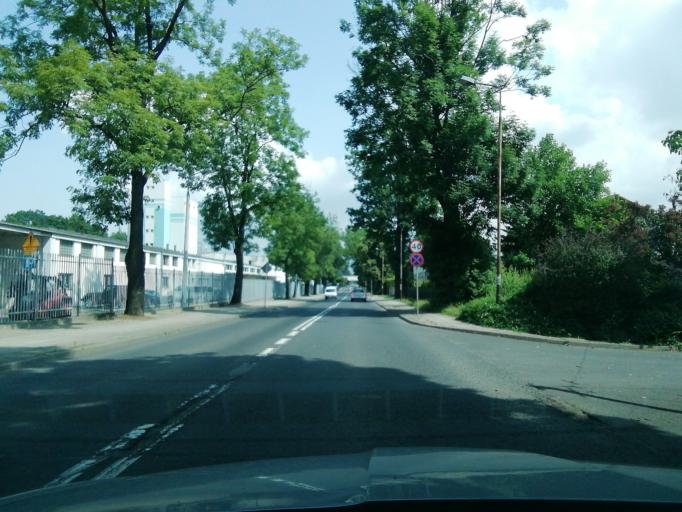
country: PL
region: Silesian Voivodeship
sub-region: Powiat zywiecki
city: Wieprz
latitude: 49.6598
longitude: 19.1728
